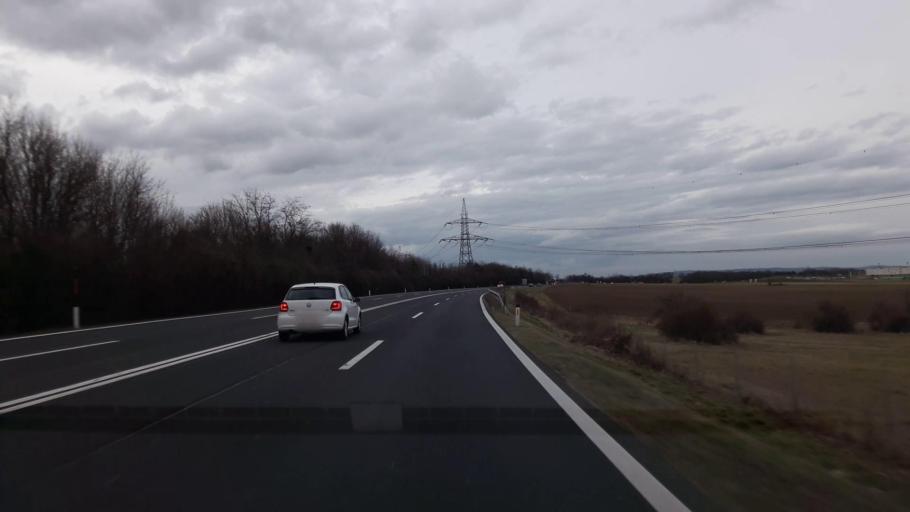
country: AT
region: Burgenland
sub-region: Politischer Bezirk Mattersburg
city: Mattersburg
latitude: 47.7352
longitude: 16.3720
